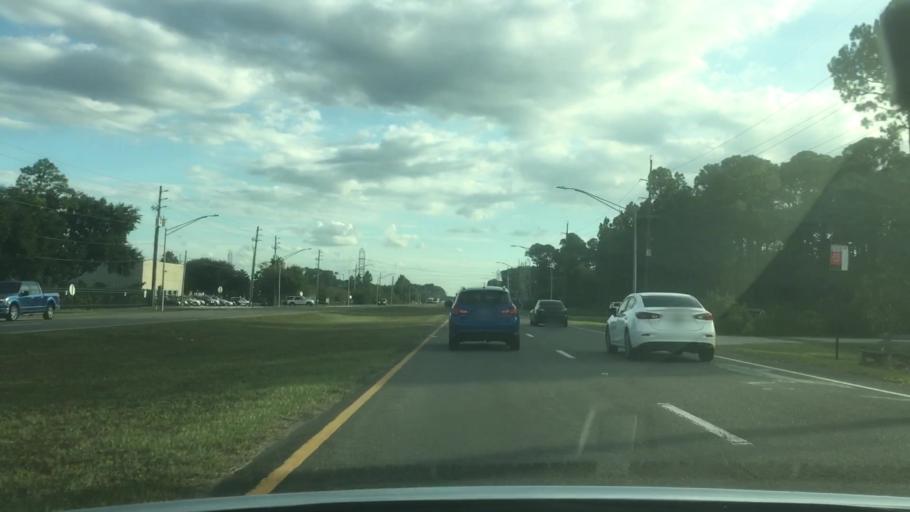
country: US
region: Florida
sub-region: Duval County
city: Neptune Beach
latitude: 30.3065
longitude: -81.5261
